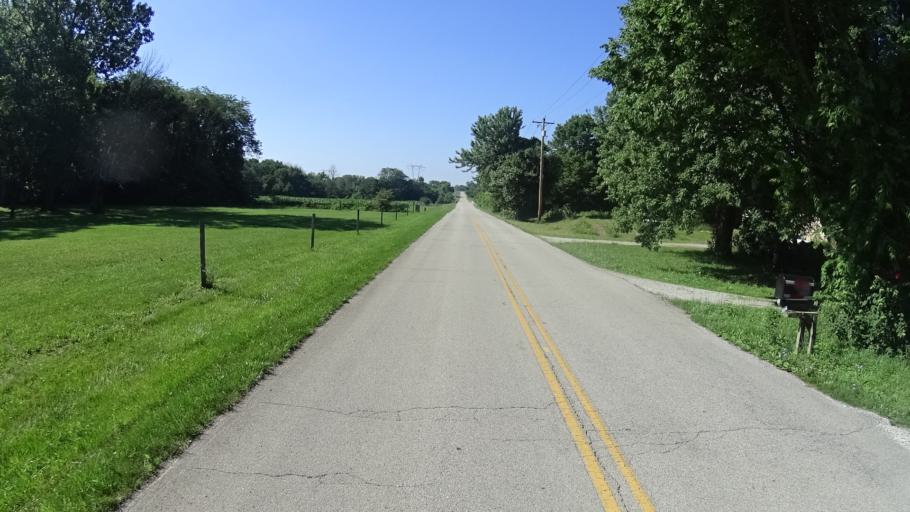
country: US
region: Indiana
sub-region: Madison County
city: Ingalls
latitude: 39.9738
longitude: -85.7962
